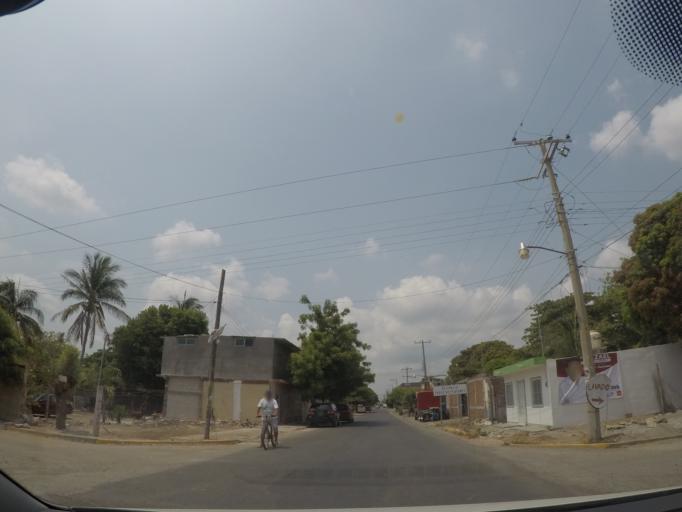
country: MX
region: Oaxaca
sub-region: El Espinal
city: El Espinal
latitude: 16.4907
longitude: -95.0440
